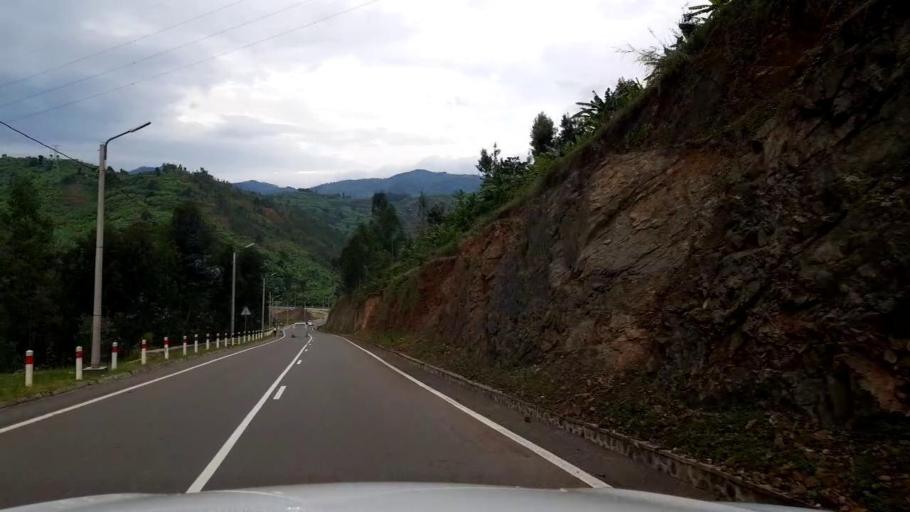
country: RW
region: Western Province
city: Kibuye
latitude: -2.0340
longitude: 29.3982
